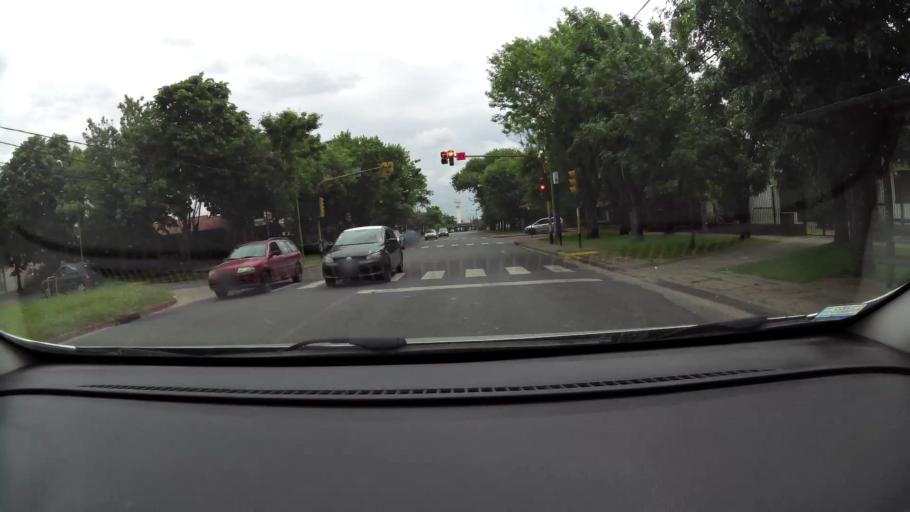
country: AR
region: Buenos Aires
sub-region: Partido de Campana
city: Campana
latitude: -34.1625
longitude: -58.9757
